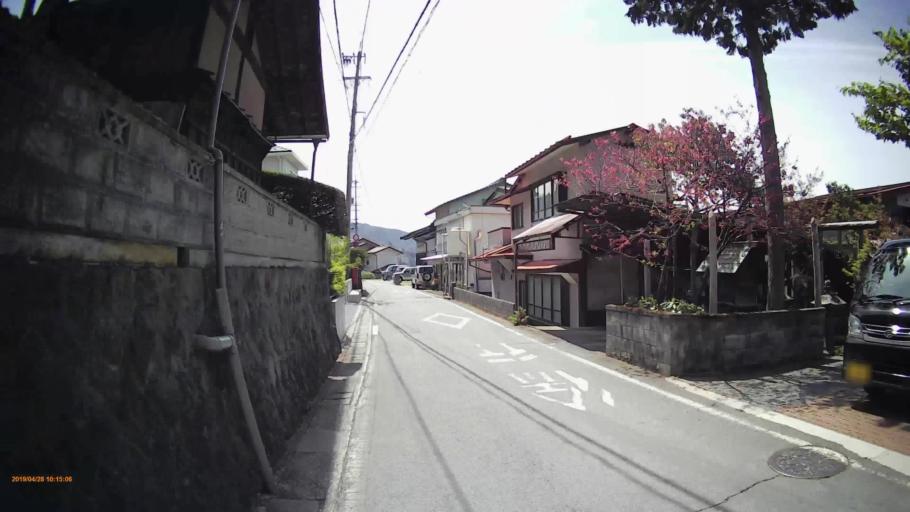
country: JP
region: Nagano
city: Suwa
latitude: 36.0649
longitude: 138.1072
